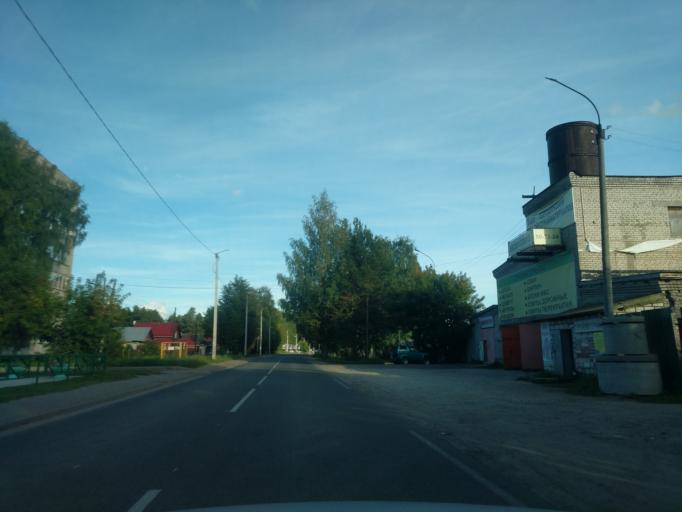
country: RU
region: Kirov
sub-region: Kirovo-Chepetskiy Rayon
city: Kirov
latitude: 58.6080
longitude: 49.8054
